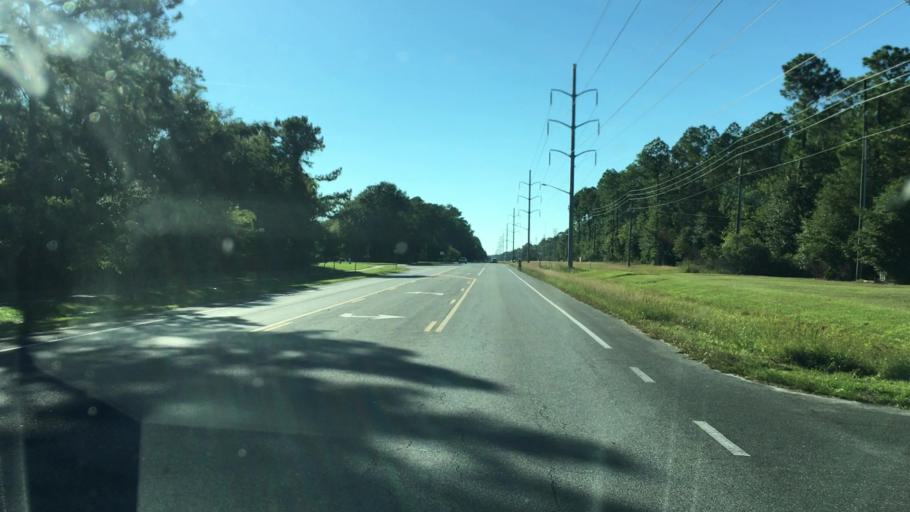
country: US
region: Florida
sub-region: Alachua County
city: Gainesville
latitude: 29.7033
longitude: -82.3520
